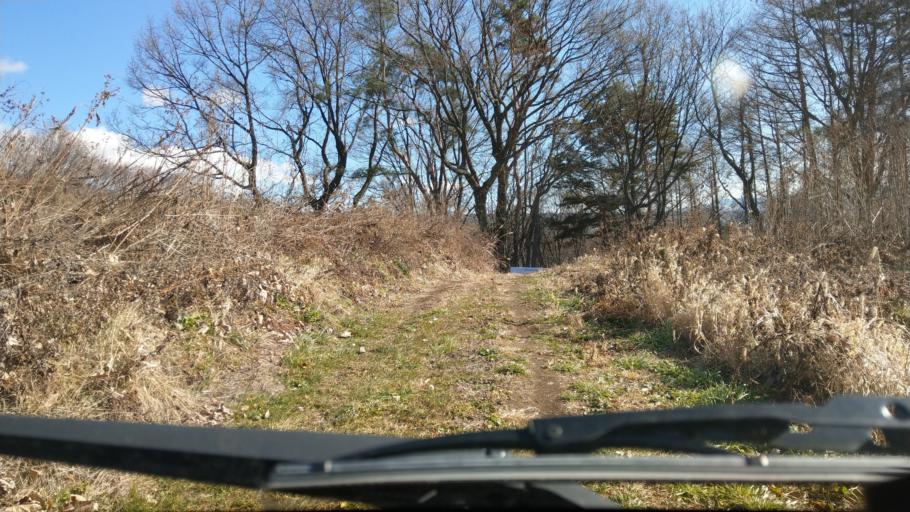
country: JP
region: Nagano
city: Komoro
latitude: 36.3616
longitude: 138.4302
